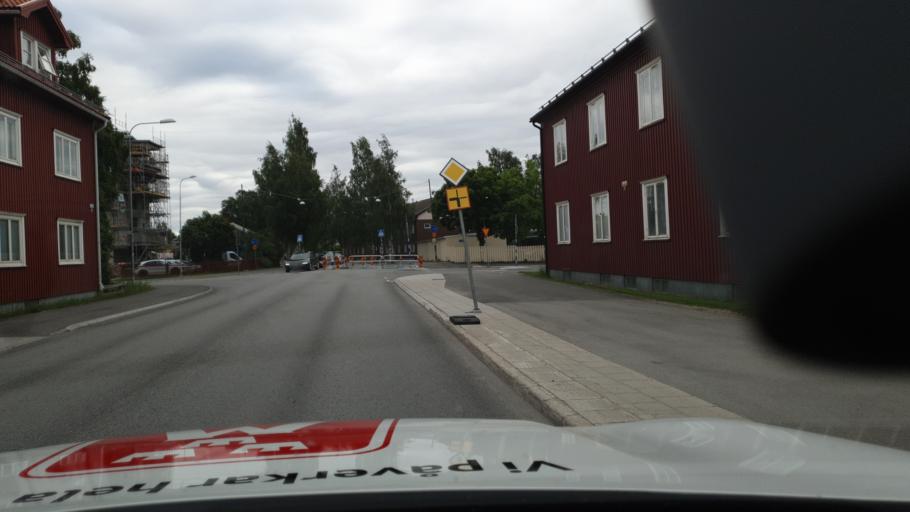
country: SE
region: Vaesterbotten
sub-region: Umea Kommun
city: Umea
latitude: 63.8304
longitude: 20.2311
